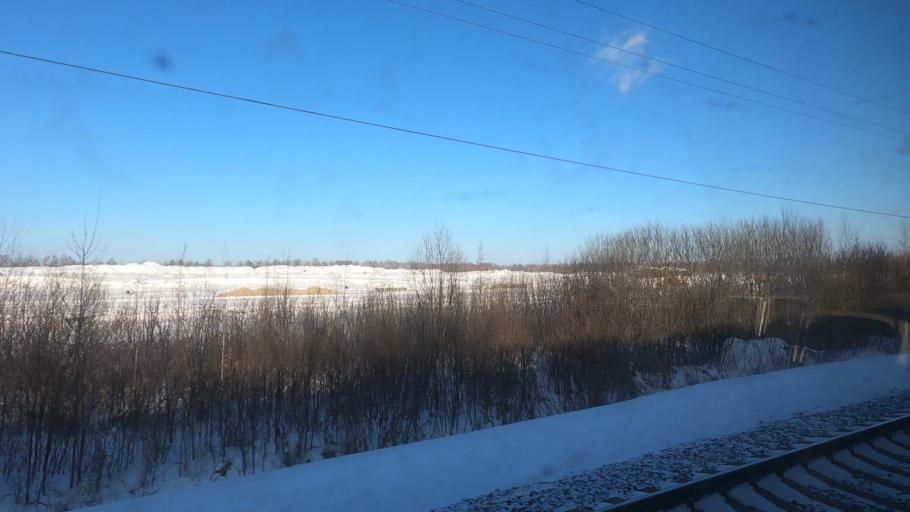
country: RU
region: Moskovskaya
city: Elektrougli
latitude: 55.7228
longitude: 38.2637
